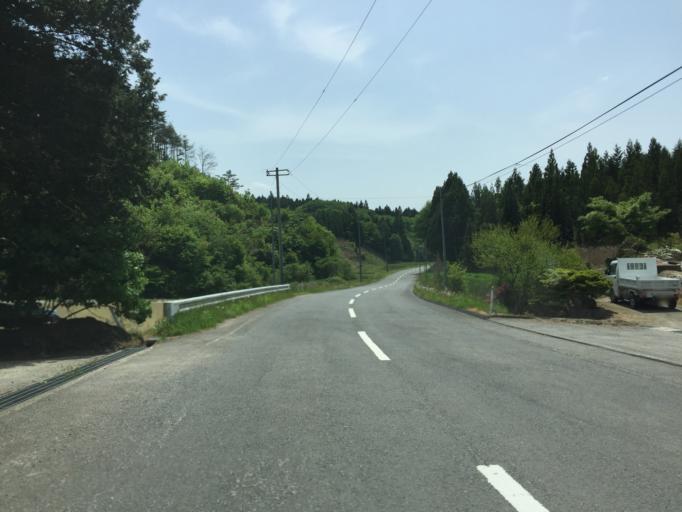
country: JP
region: Fukushima
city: Ishikawa
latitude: 37.1851
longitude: 140.5327
